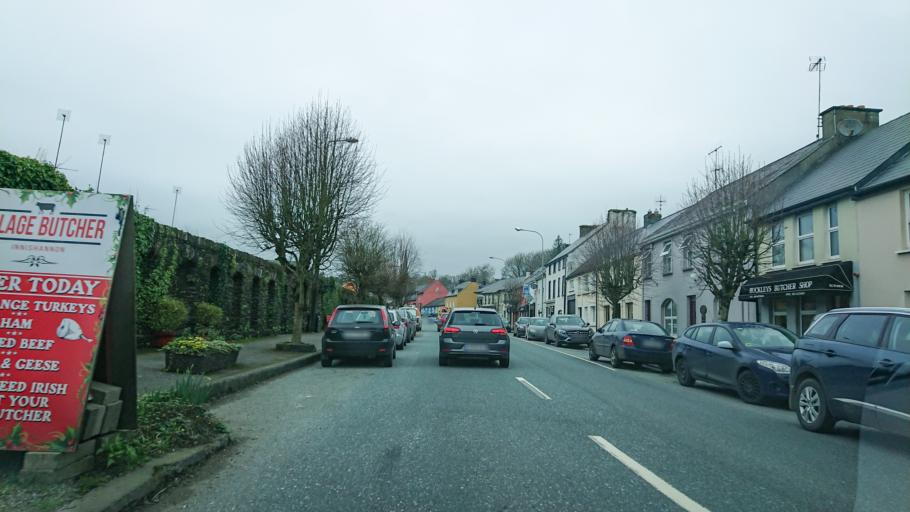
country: IE
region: Munster
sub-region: County Cork
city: Bandon
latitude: 51.7644
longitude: -8.6560
